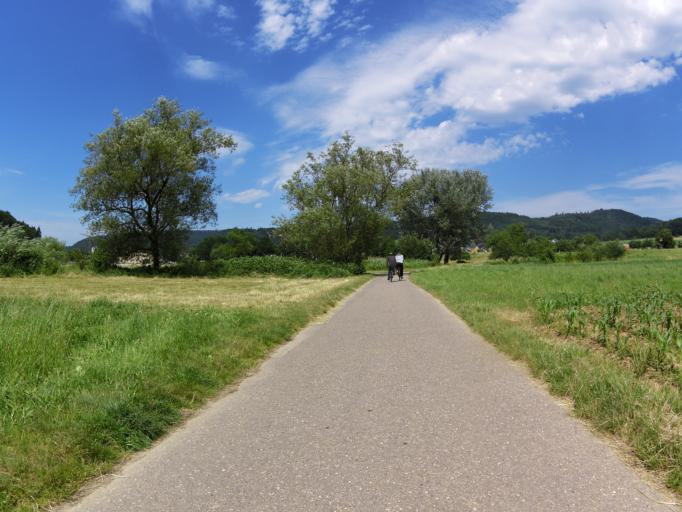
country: DE
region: Baden-Wuerttemberg
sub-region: Freiburg Region
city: Seelbach
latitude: 48.3217
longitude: 7.9353
